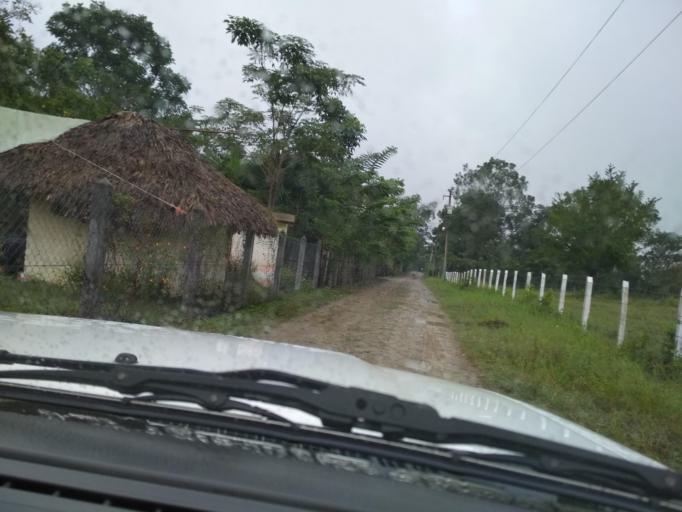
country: MX
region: Veracruz
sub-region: Chalma
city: San Pedro Coyutla
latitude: 21.2479
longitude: -98.4629
